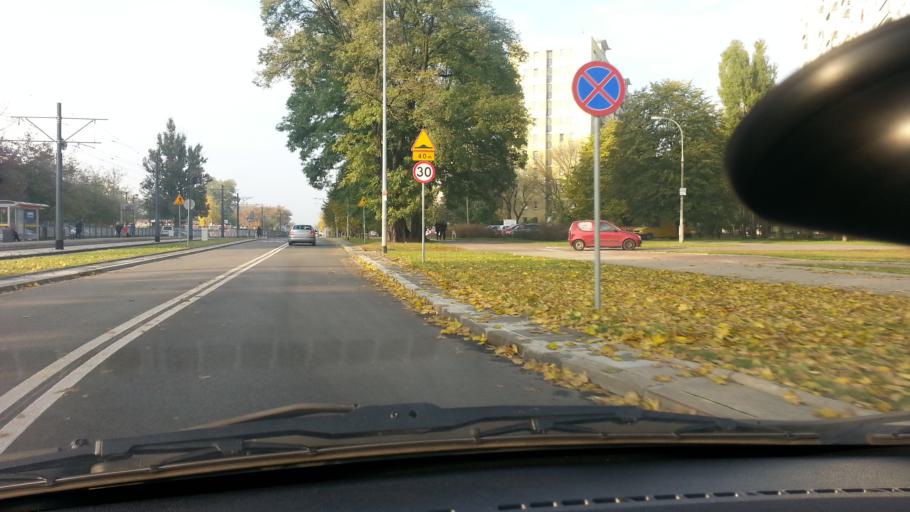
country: PL
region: Masovian Voivodeship
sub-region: Warszawa
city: Targowek
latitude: 52.2837
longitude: 21.0340
